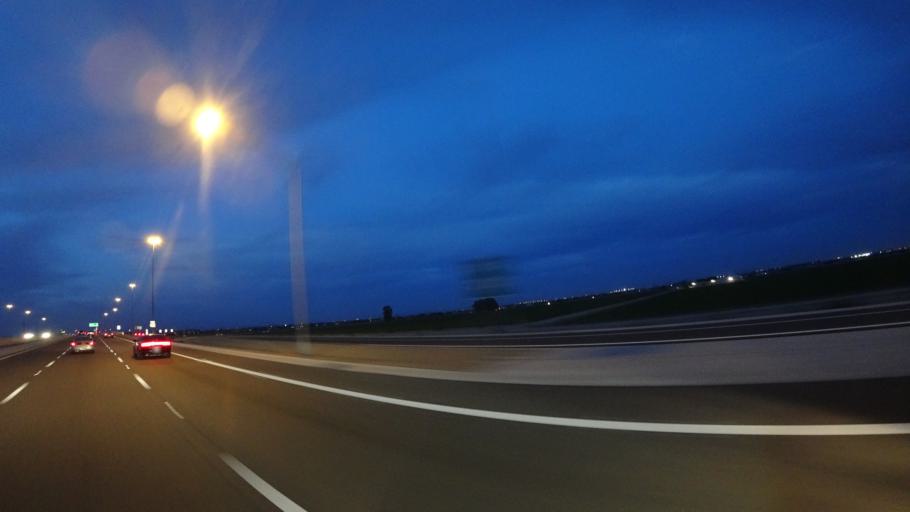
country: US
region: Arizona
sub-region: Maricopa County
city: Citrus Park
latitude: 33.5767
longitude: -112.4180
